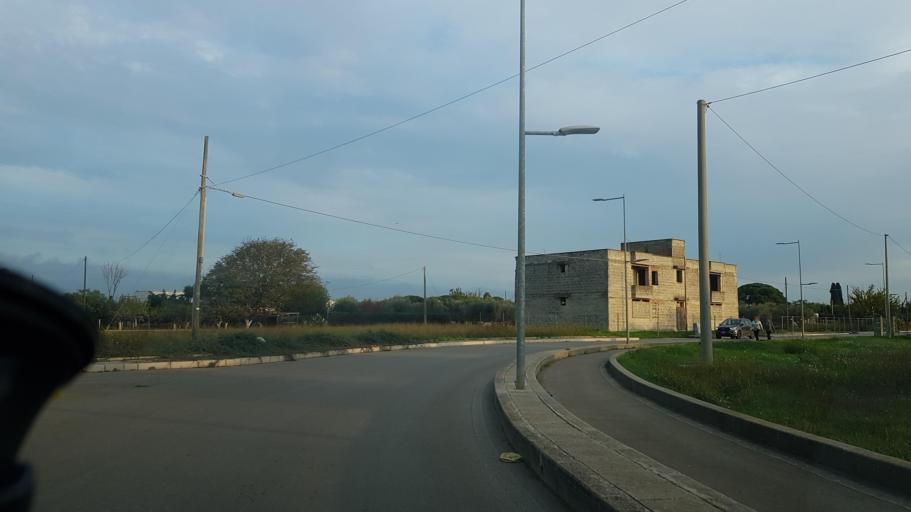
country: IT
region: Apulia
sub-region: Provincia di Brindisi
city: Latiano
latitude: 40.5585
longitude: 17.7225
